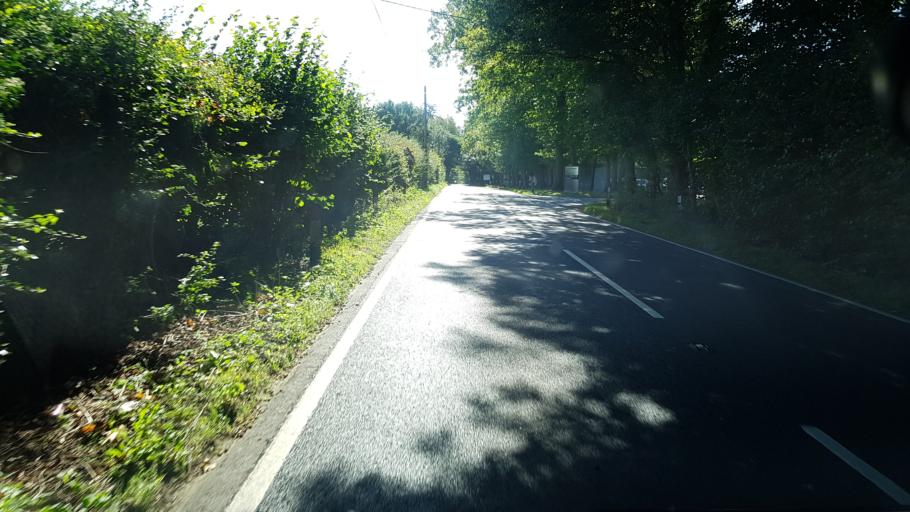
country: GB
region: England
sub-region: Kent
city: Borough Green
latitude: 51.2799
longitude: 0.3523
